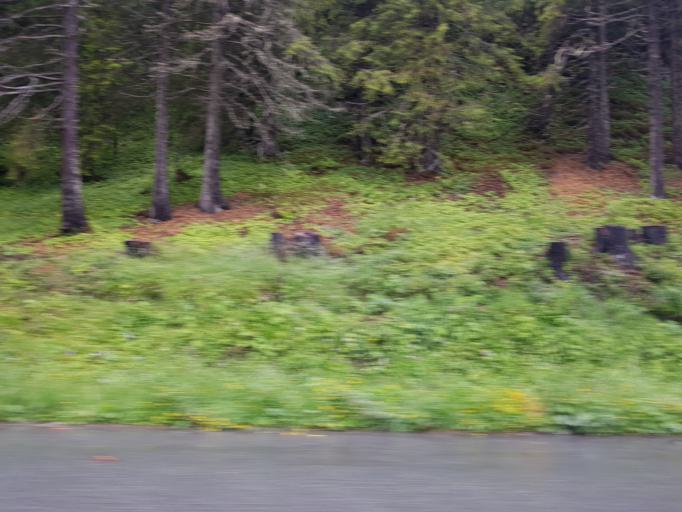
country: NO
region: Sor-Trondelag
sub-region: Selbu
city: Mebonden
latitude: 63.3316
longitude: 11.0907
